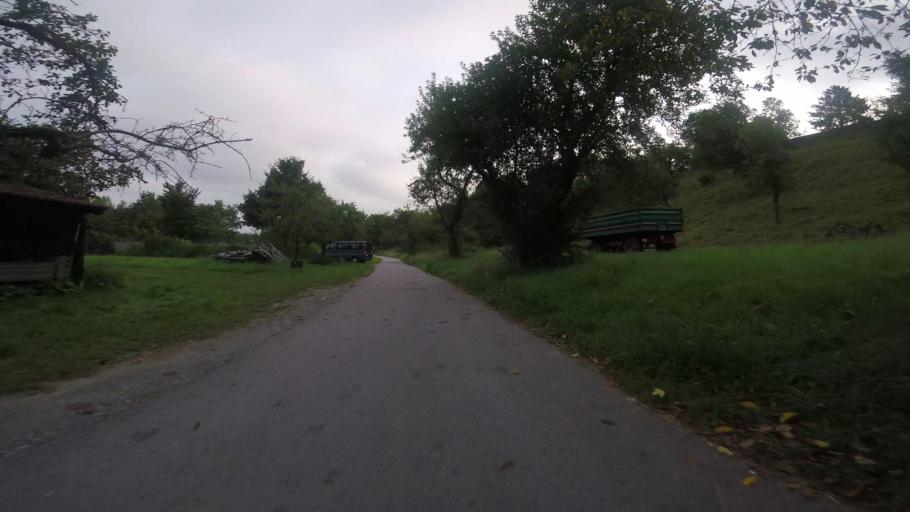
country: DE
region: Baden-Wuerttemberg
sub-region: Regierungsbezirk Stuttgart
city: Oberstenfeld
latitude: 49.0285
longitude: 9.3213
